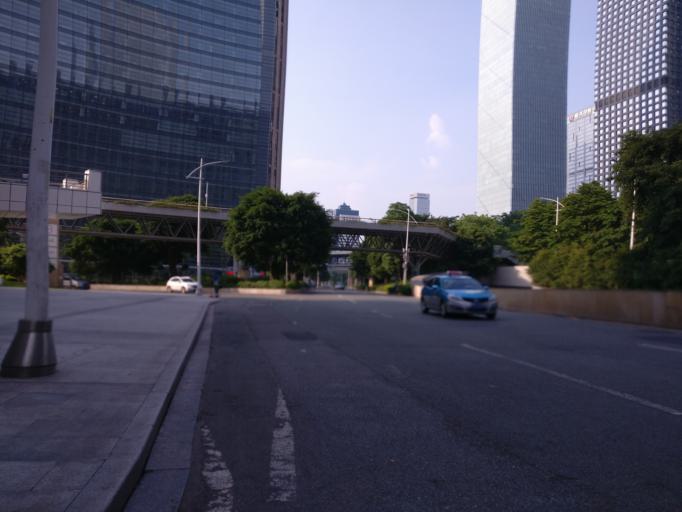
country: CN
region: Guangdong
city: Wushan
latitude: 23.1255
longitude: 113.3177
